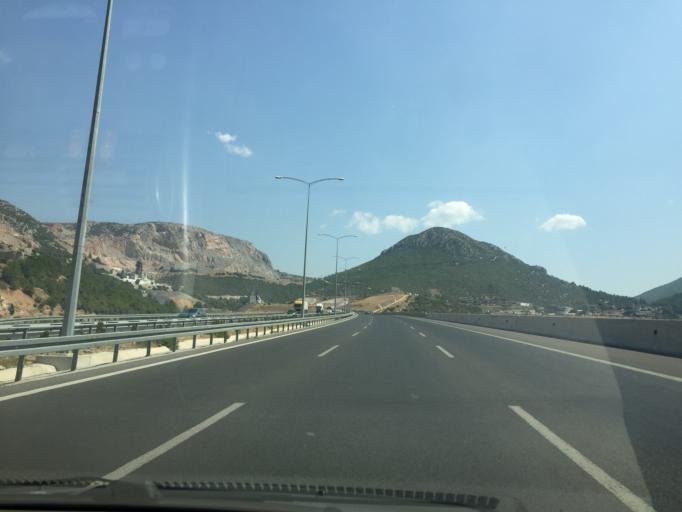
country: TR
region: Izmir
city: Bornova
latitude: 38.4517
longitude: 27.2995
